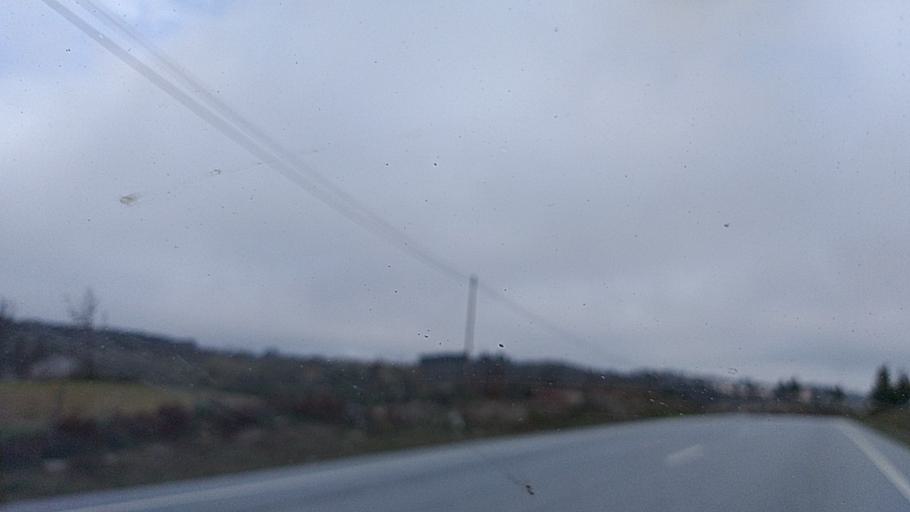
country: PT
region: Guarda
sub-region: Fornos de Algodres
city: Fornos de Algodres
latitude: 40.6718
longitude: -7.4738
